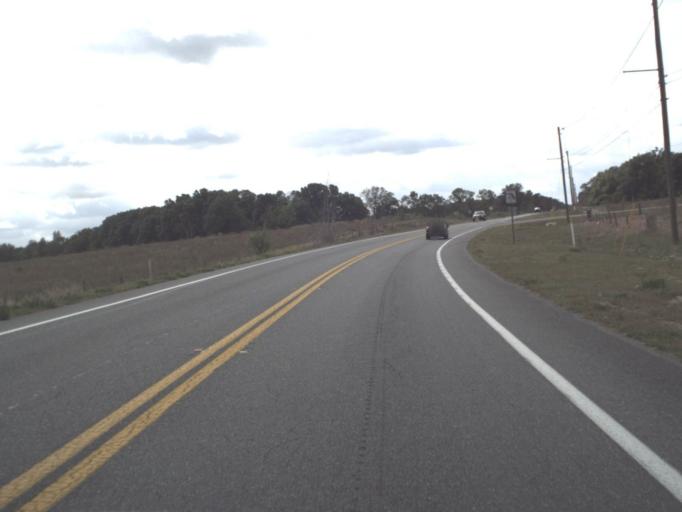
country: US
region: Florida
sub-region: Marion County
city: Ocala
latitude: 29.2585
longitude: -82.0737
